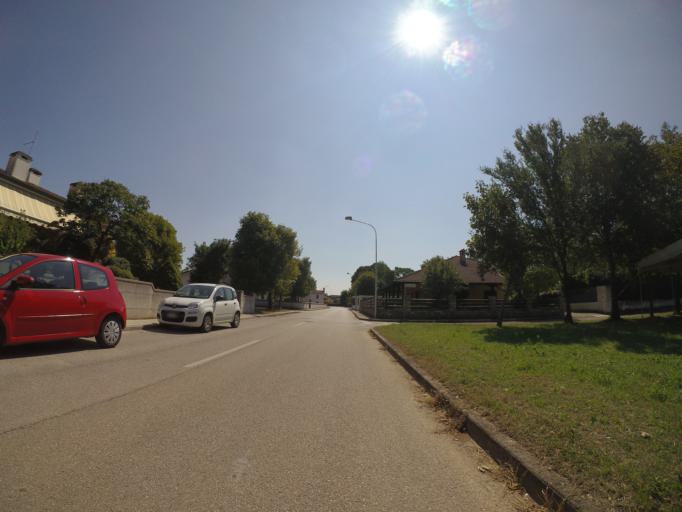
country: IT
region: Friuli Venezia Giulia
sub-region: Provincia di Udine
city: Talmassons
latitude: 45.9369
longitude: 13.0914
